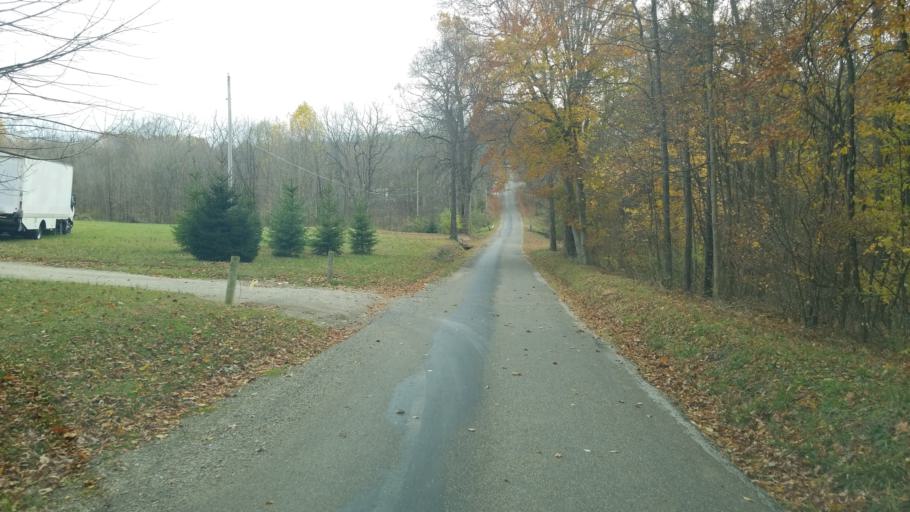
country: US
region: Ohio
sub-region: Richland County
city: Lincoln Heights
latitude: 40.7112
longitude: -82.4551
